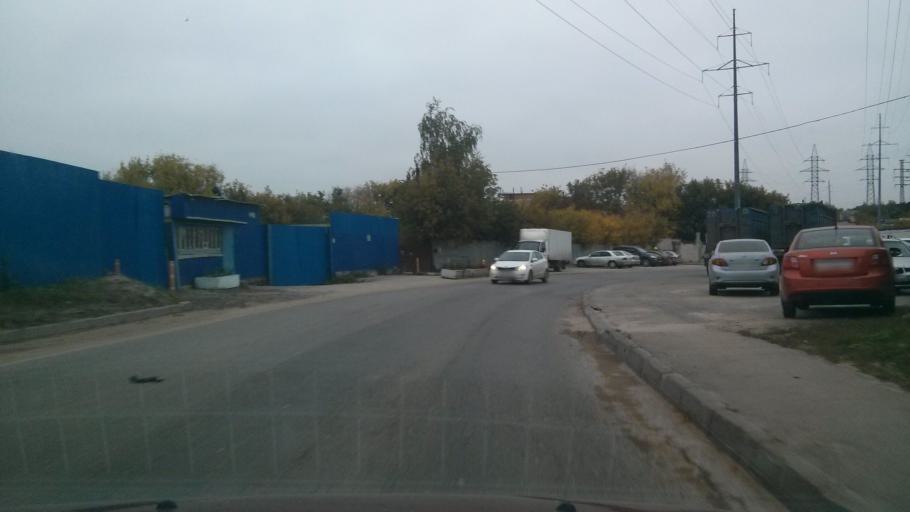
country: RU
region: Nizjnij Novgorod
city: Nizhniy Novgorod
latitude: 56.3075
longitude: 44.0102
